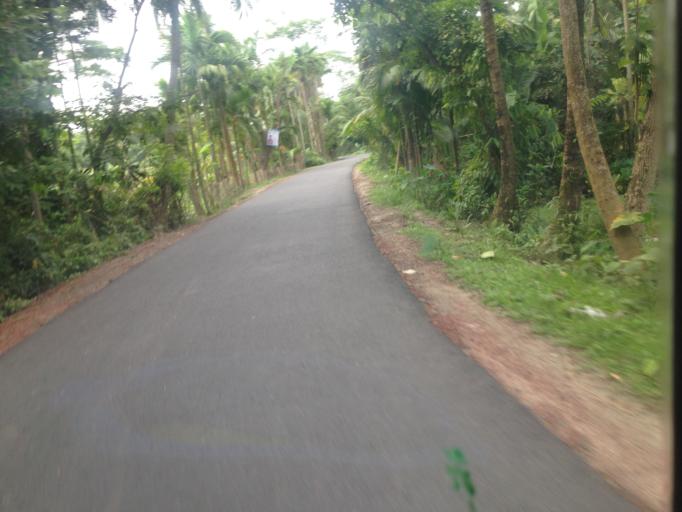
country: BD
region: Chittagong
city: Raipur
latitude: 23.0354
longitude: 90.7441
